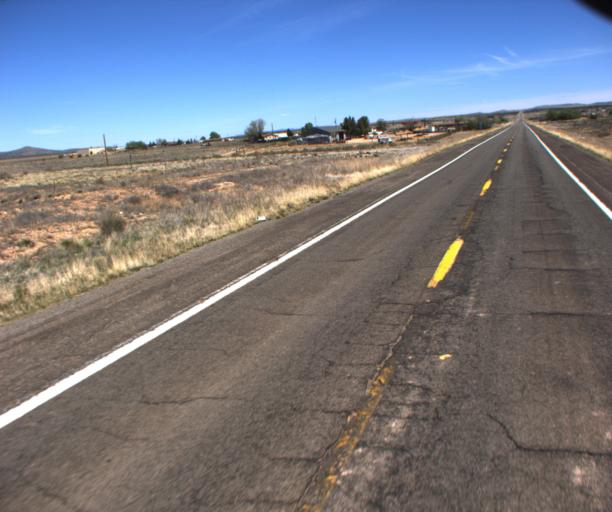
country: US
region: Arizona
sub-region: Mohave County
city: Peach Springs
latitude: 35.4808
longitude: -113.5717
